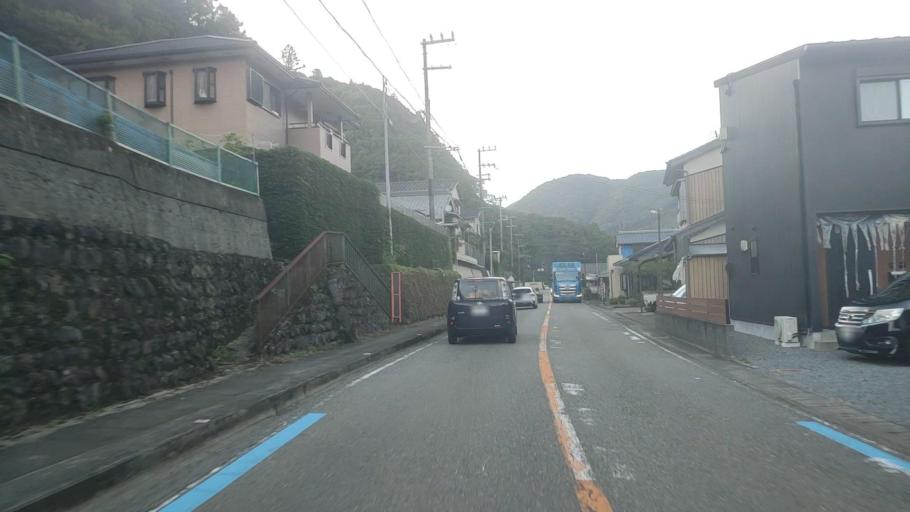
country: JP
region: Wakayama
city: Tanabe
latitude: 33.7951
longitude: 135.5185
